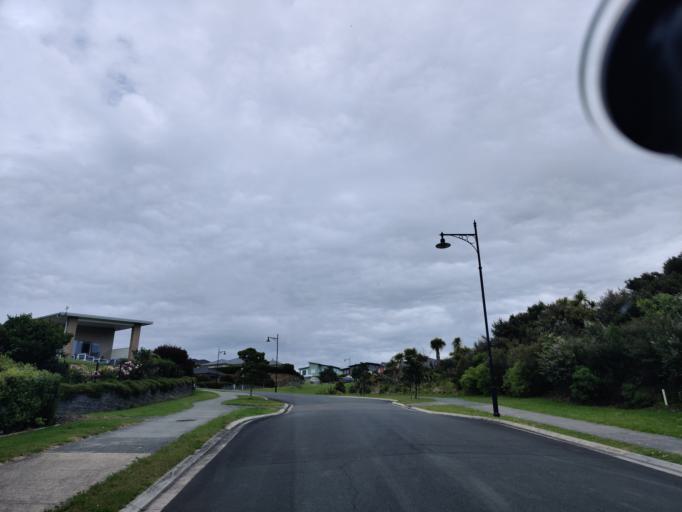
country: NZ
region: Auckland
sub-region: Auckland
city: Rothesay Bay
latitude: -36.5677
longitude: 174.6864
